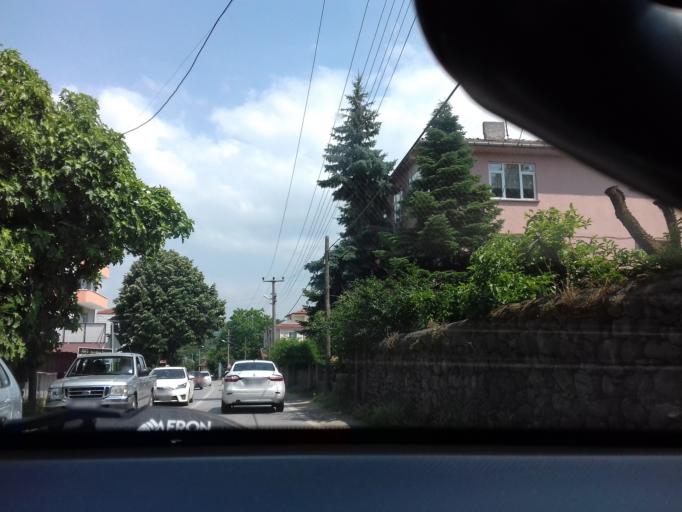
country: TR
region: Sakarya
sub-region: Merkez
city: Sapanca
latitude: 40.6884
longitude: 30.2651
